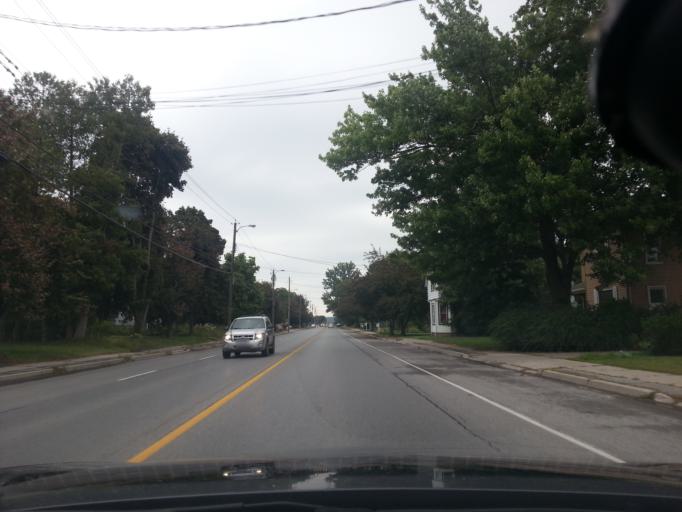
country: CA
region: Ontario
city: Picton
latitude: 44.0019
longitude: -77.1559
